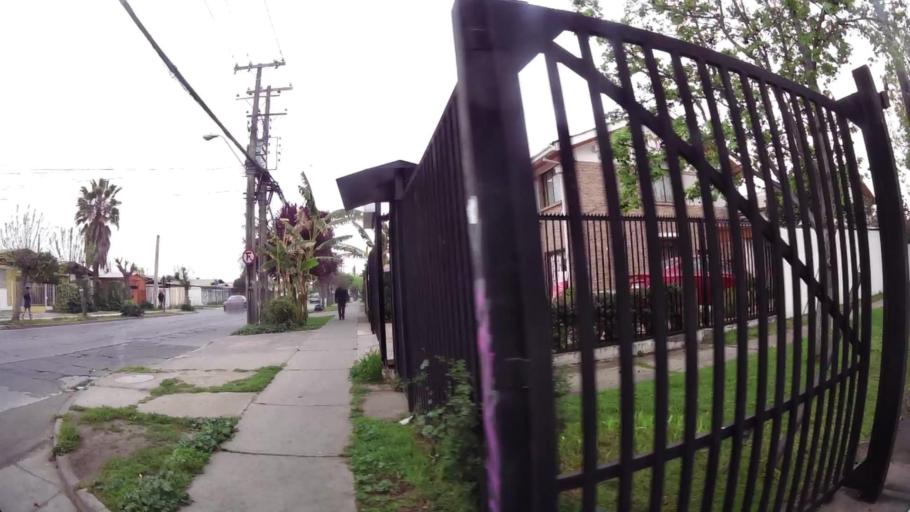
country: CL
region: Santiago Metropolitan
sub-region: Provincia de Santiago
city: Lo Prado
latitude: -33.5019
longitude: -70.7456
